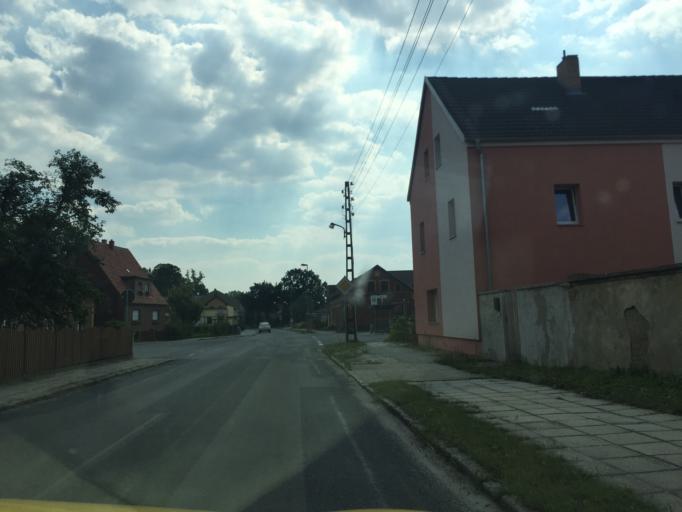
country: DE
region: Brandenburg
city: Welzow
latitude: 51.5734
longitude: 14.1730
